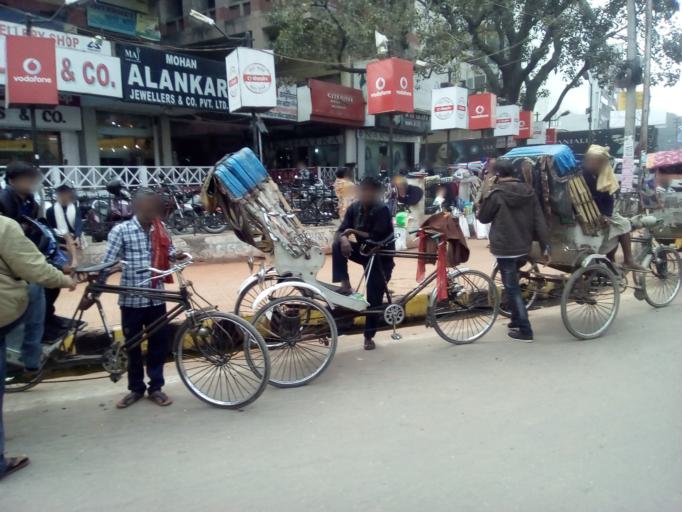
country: IN
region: Bihar
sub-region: Patna
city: Patna
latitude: 25.6100
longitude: 85.1374
